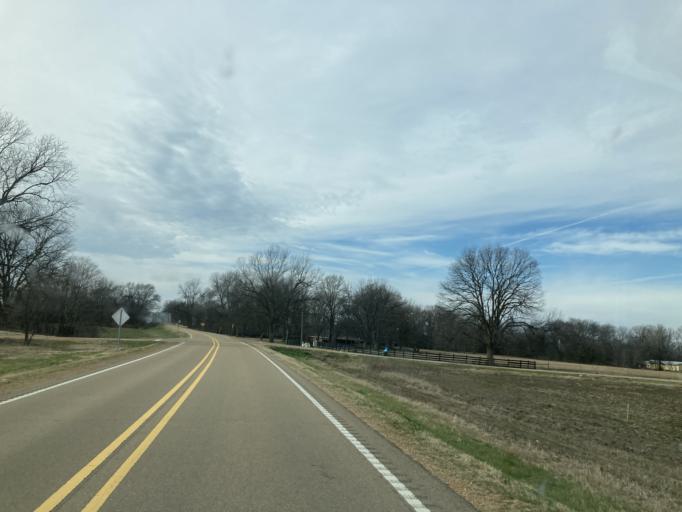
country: US
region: Mississippi
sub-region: Washington County
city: Hollandale
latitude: 33.1845
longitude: -90.6814
